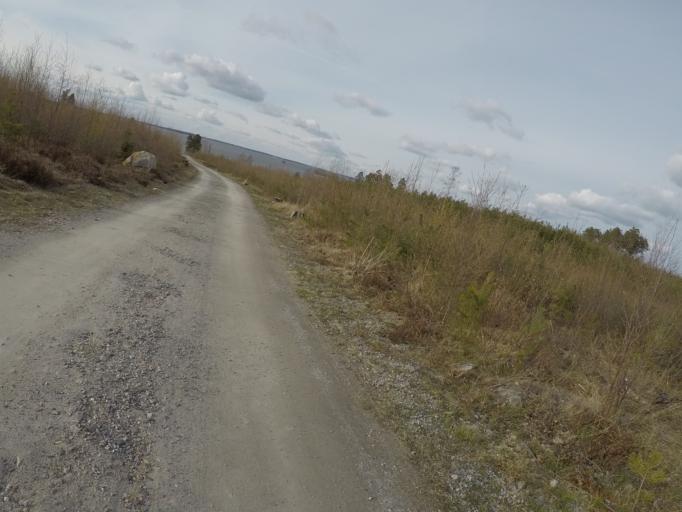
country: SE
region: Soedermanland
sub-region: Eskilstuna Kommun
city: Torshalla
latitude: 59.4485
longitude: 16.5474
